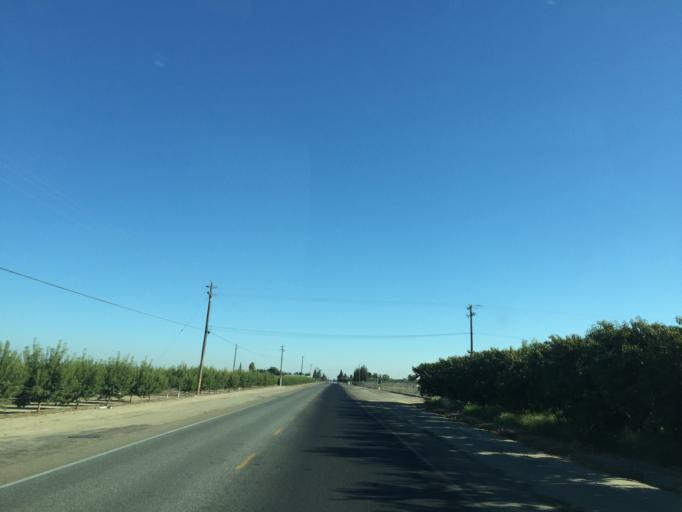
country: US
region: California
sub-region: Tulare County
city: London
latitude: 36.5070
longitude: -119.4489
